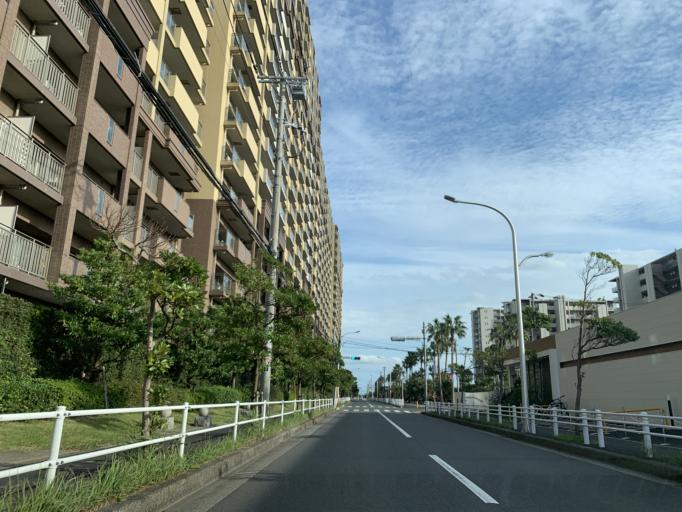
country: JP
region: Tokyo
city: Urayasu
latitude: 35.6348
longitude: 139.9132
